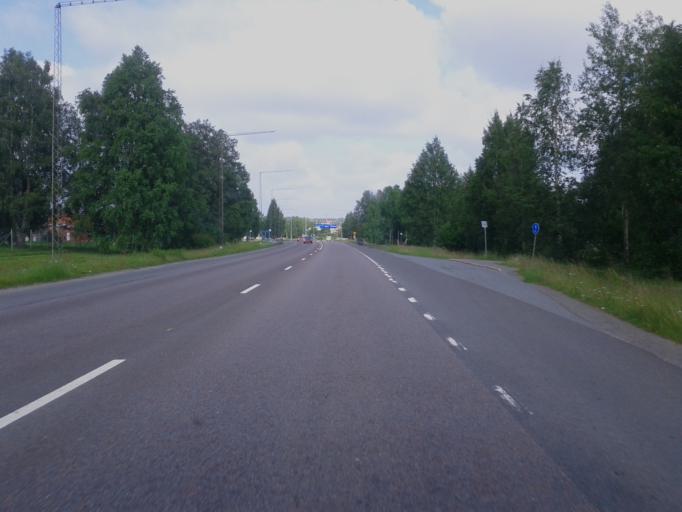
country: SE
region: Vaesterbotten
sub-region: Skelleftea Kommun
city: Skelleftea
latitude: 64.7403
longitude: 20.9635
